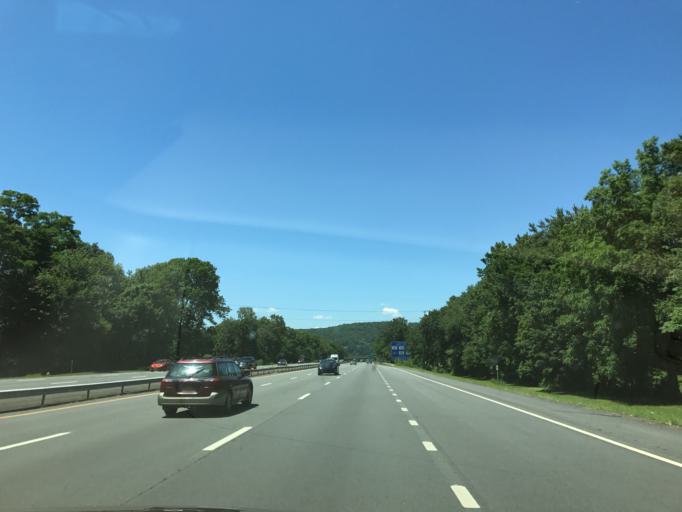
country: US
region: New York
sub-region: Rockland County
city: Airmont
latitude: 41.1182
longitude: -74.1202
